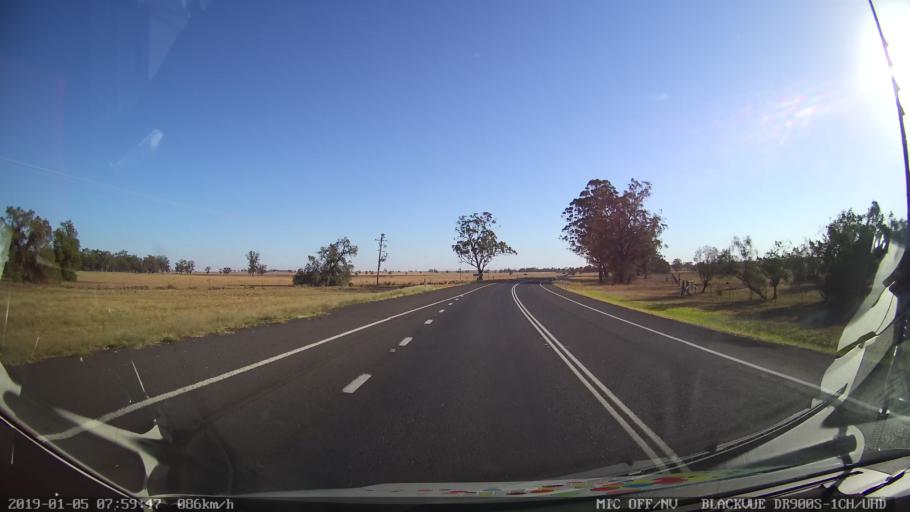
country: AU
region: New South Wales
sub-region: Gilgandra
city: Gilgandra
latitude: -31.6978
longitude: 148.6800
